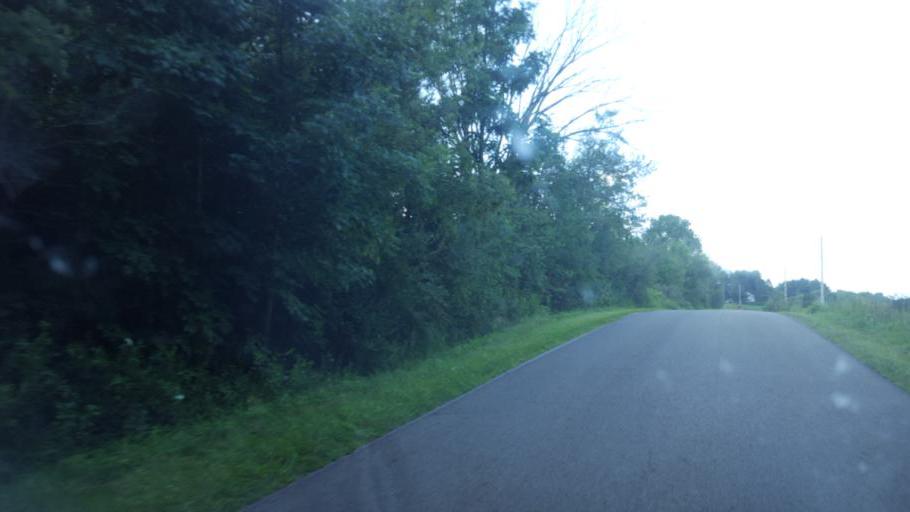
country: US
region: Ohio
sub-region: Knox County
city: Centerburg
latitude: 40.4099
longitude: -82.6751
